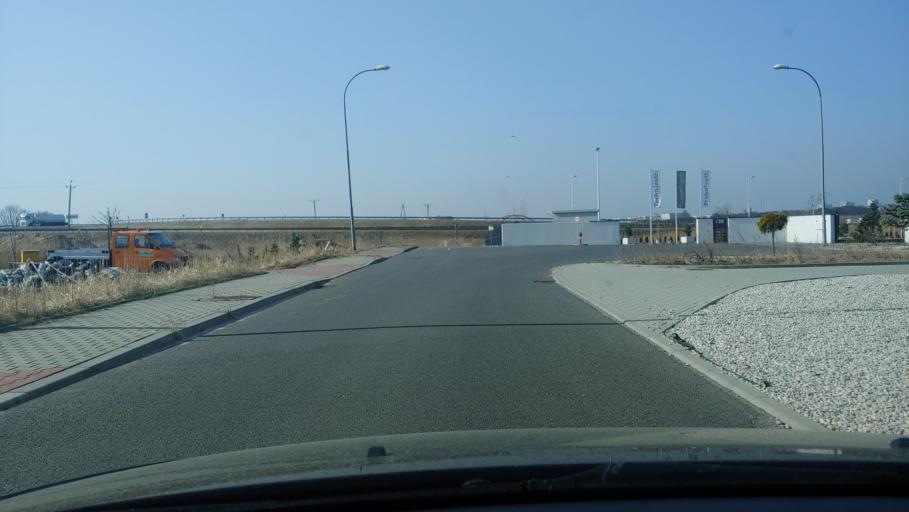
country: PL
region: Lesser Poland Voivodeship
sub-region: Powiat chrzanowski
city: Chrzanow
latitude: 50.1503
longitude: 19.4314
